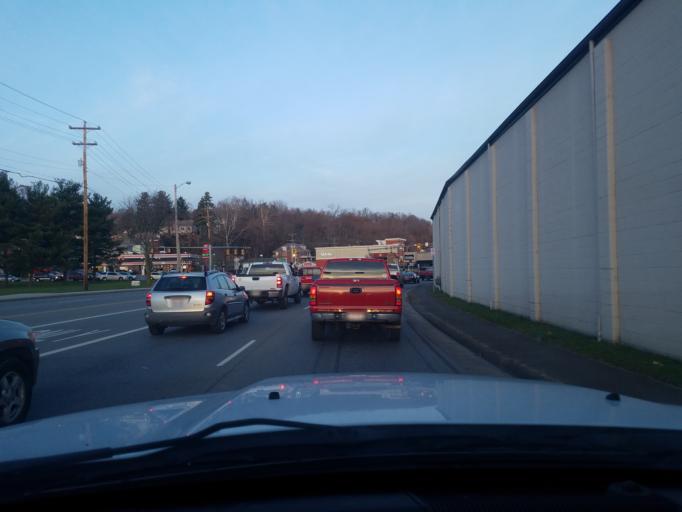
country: US
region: Ohio
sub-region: Washington County
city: Marietta
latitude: 39.4147
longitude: -81.4453
